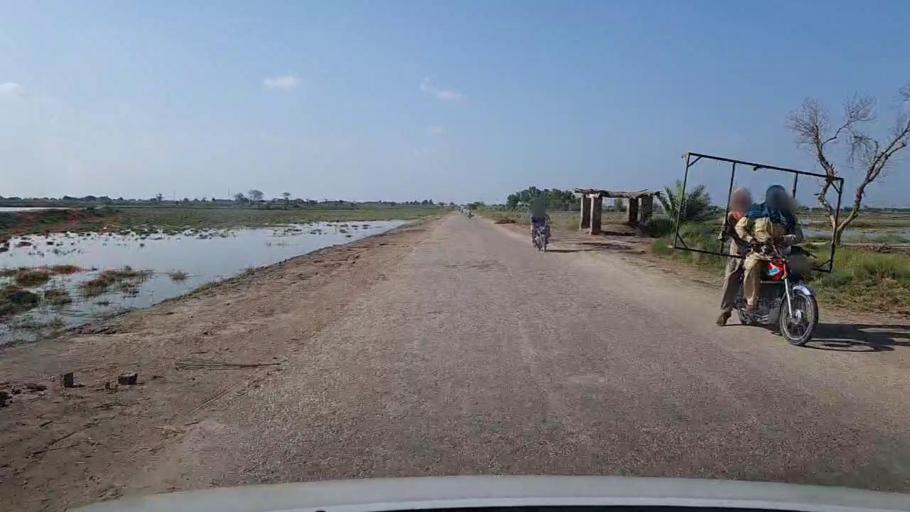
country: PK
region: Sindh
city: Kandiaro
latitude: 27.0611
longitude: 68.3162
